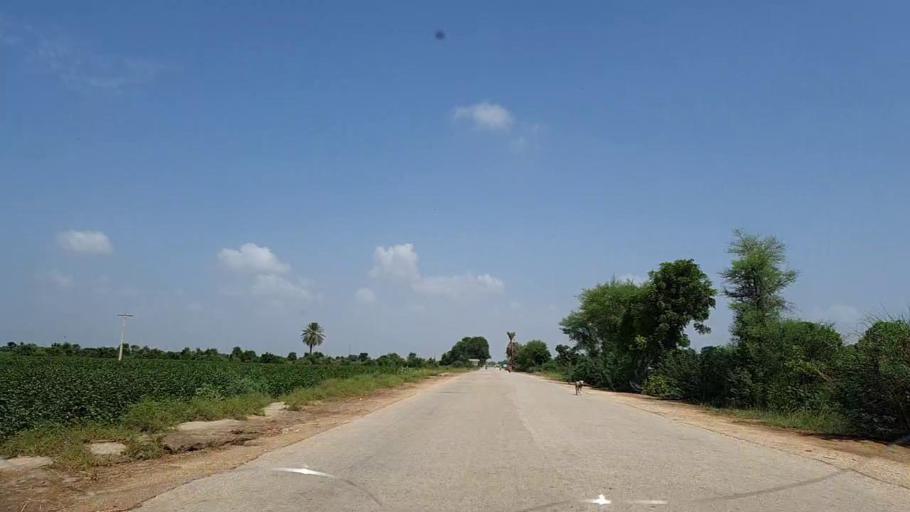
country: PK
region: Sindh
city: Pad Idan
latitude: 26.7888
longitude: 68.2595
